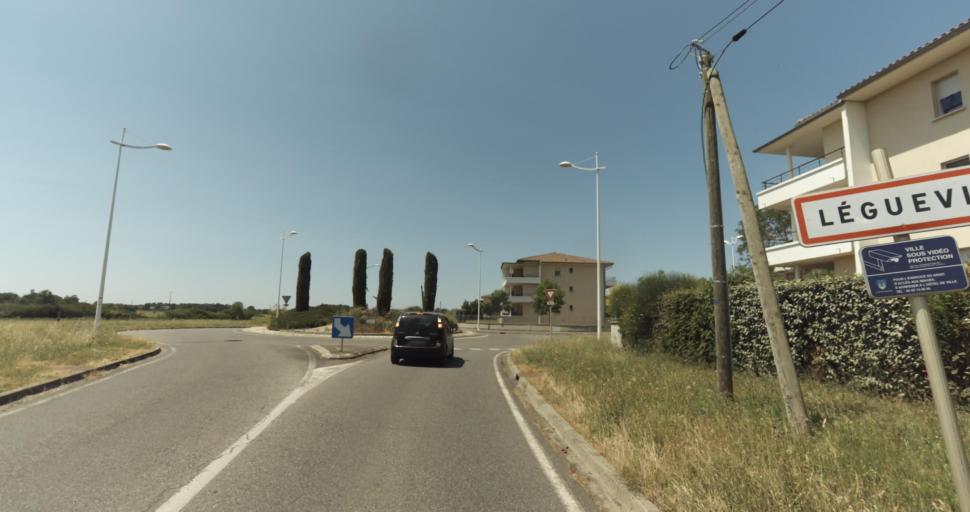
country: FR
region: Midi-Pyrenees
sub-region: Departement de la Haute-Garonne
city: La Salvetat-Saint-Gilles
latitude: 43.5992
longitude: 1.2630
